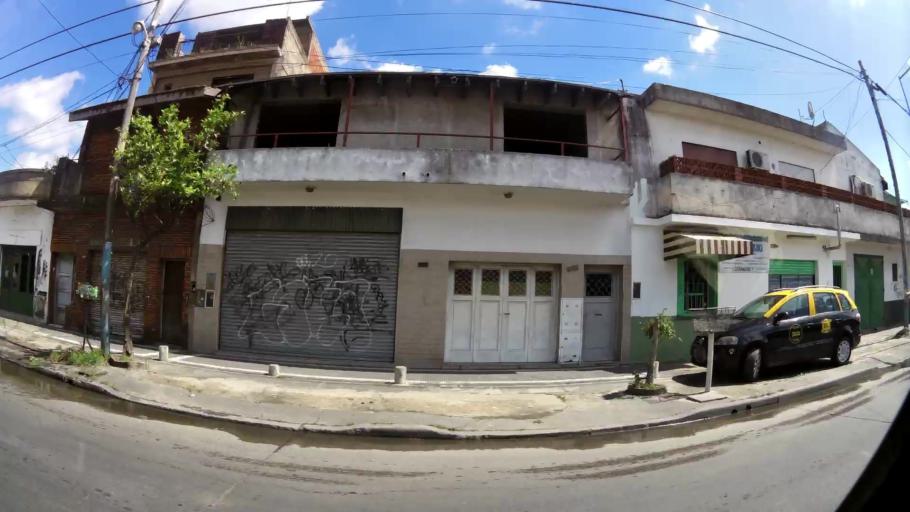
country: AR
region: Buenos Aires
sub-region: Partido de Lanus
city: Lanus
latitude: -34.6736
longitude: -58.4270
